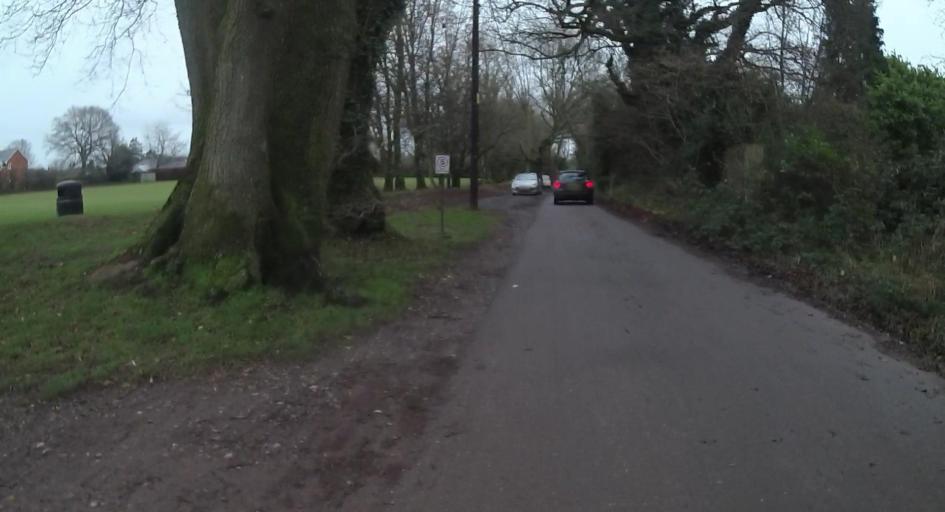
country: GB
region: England
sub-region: Hampshire
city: Four Marks
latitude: 51.1044
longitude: -1.0549
